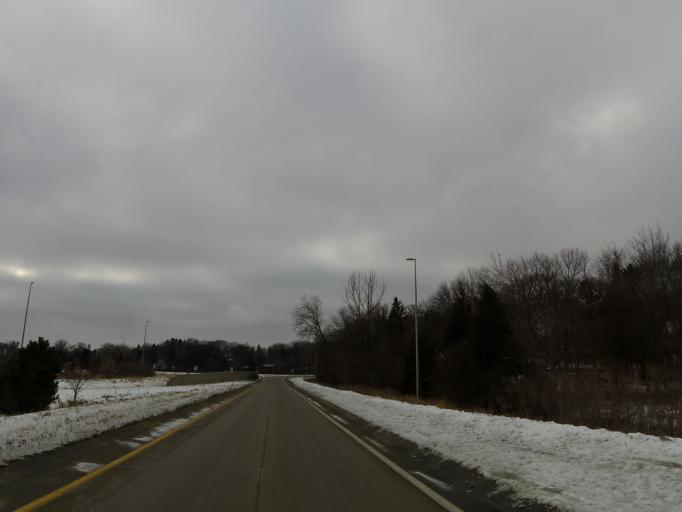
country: US
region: Minnesota
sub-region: Hennepin County
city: Hopkins
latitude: 44.9265
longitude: -93.4529
